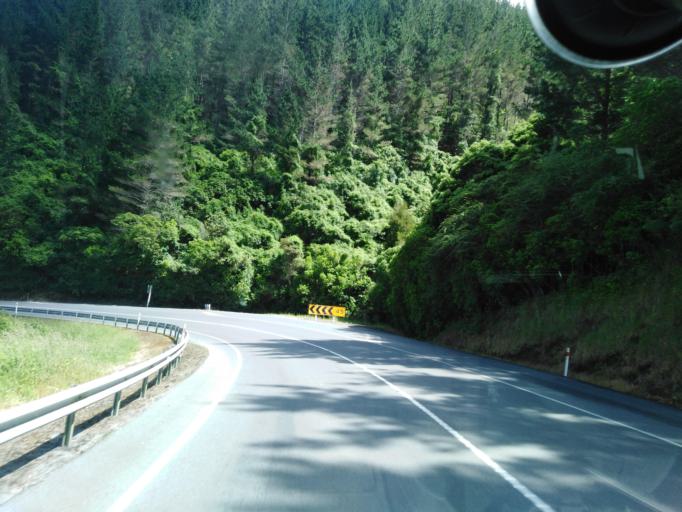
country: NZ
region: Nelson
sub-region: Nelson City
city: Nelson
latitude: -41.2263
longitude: 173.4198
